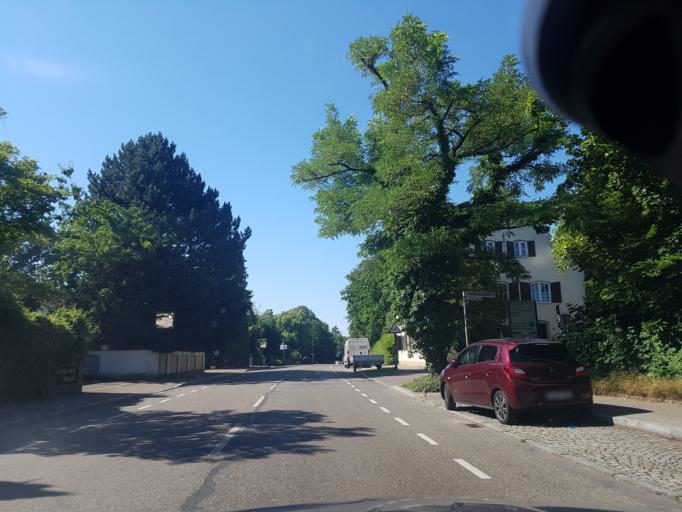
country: DE
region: Bavaria
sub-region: Swabia
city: Guenzburg
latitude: 48.4499
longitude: 10.2804
